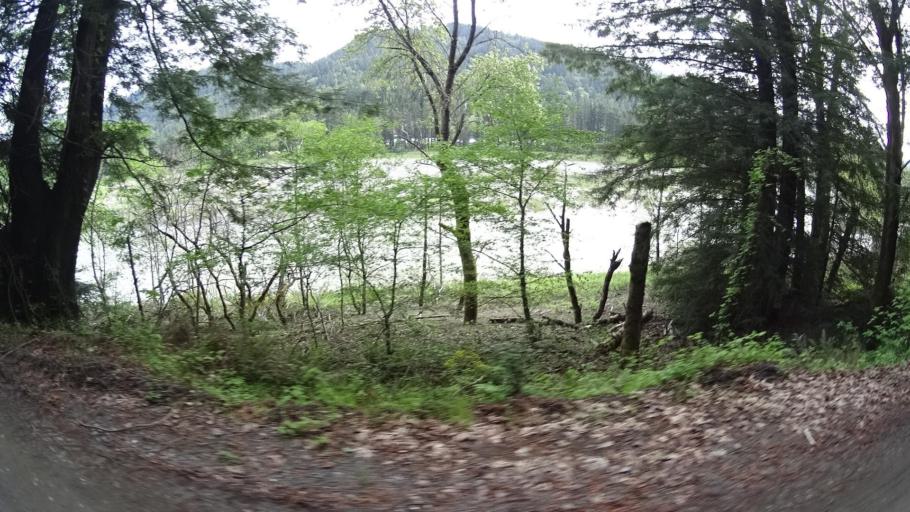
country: US
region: California
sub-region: Humboldt County
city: Redway
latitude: 40.3262
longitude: -123.8405
